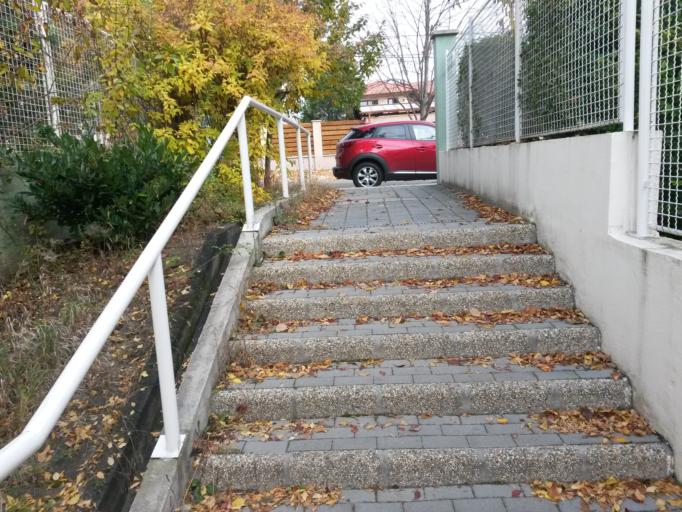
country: HU
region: Budapest
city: Budapest XII. keruelet
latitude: 47.4730
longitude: 18.9992
